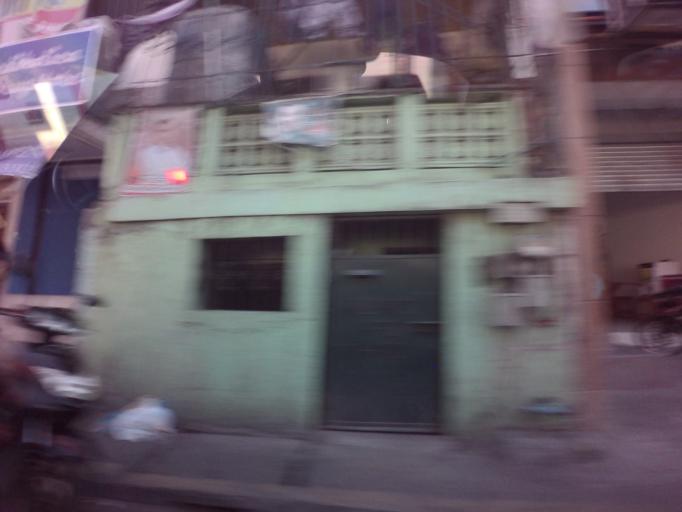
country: PH
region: Calabarzon
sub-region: Province of Rizal
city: Taguig
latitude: 14.4902
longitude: 121.0473
